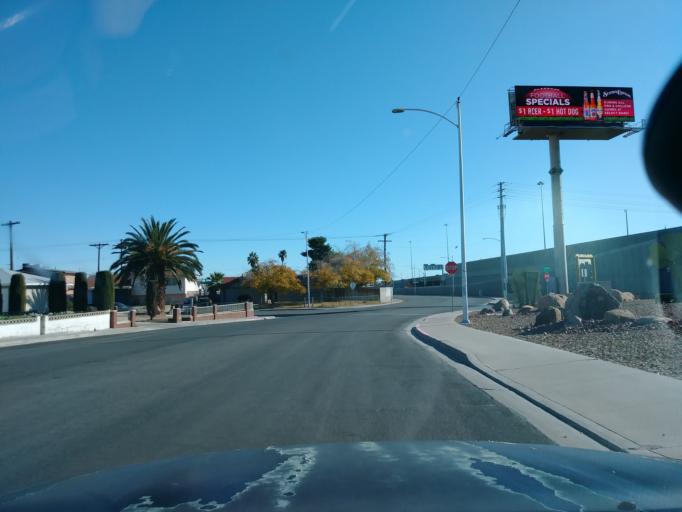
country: US
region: Nevada
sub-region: Clark County
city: Spring Valley
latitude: 36.1750
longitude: -115.2269
